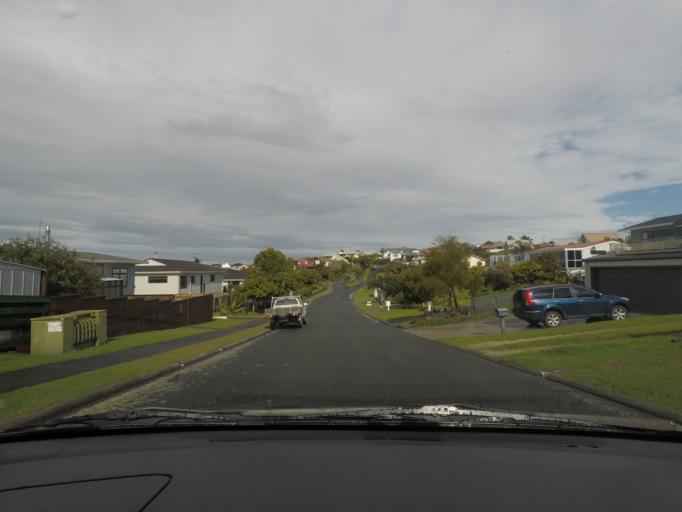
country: NZ
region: Auckland
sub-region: Auckland
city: Warkworth
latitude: -36.4144
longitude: 174.7256
